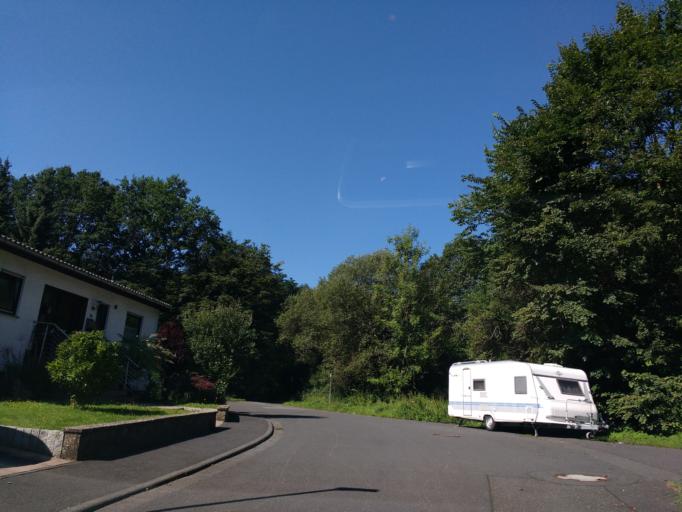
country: DE
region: Hesse
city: Herborn
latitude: 50.6754
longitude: 8.2961
